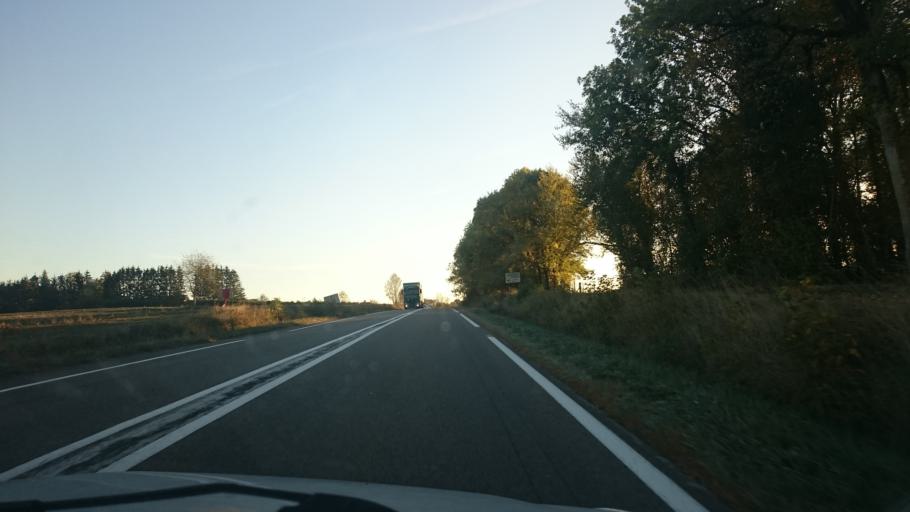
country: FR
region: Franche-Comte
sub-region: Departement du Doubs
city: Quingey
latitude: 47.0567
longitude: 5.8811
